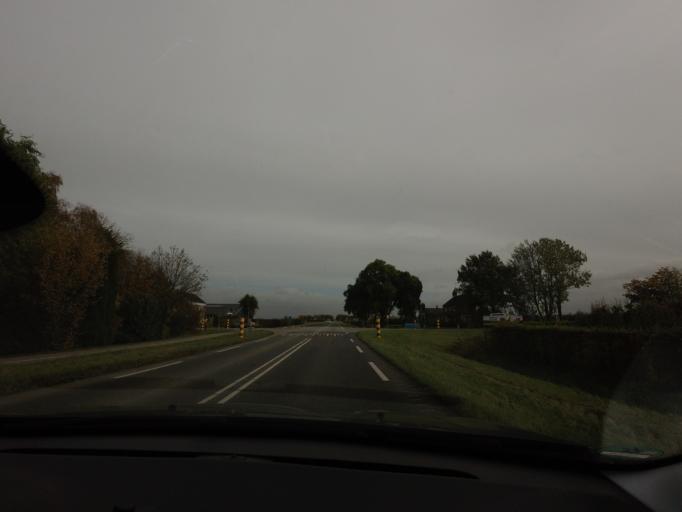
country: NL
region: Overijssel
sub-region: Gemeente Steenwijkerland
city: Blokzijl
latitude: 52.7170
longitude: 5.8994
